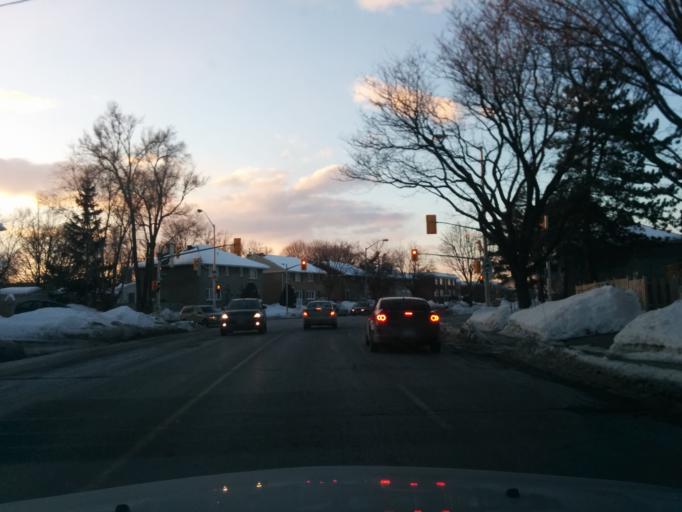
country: CA
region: Ontario
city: Ottawa
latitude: 45.3798
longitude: -75.7368
